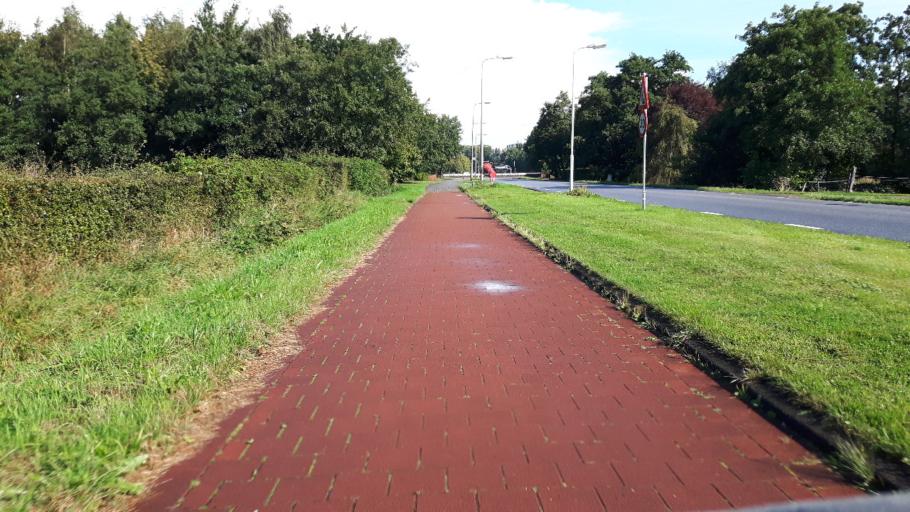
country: NL
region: Friesland
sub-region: Gemeente Smallingerland
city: Drachten
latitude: 53.0908
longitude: 6.0995
